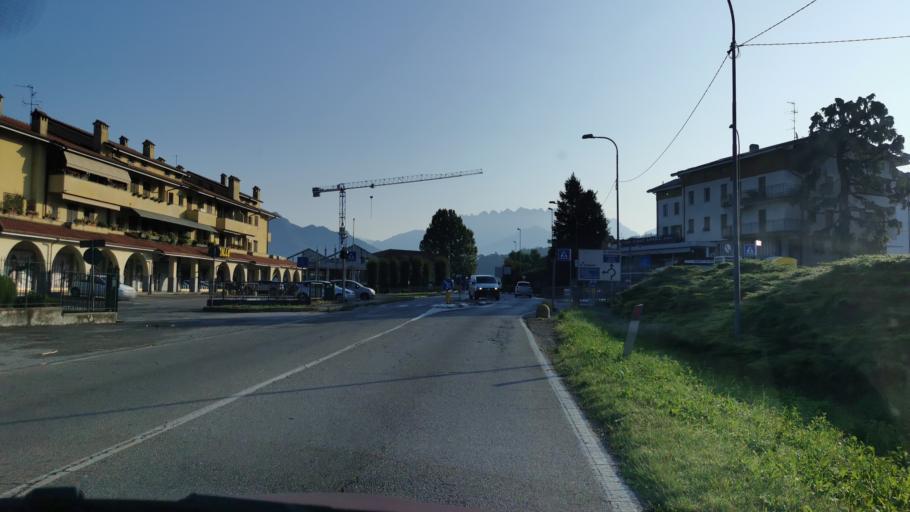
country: IT
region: Lombardy
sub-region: Provincia di Lecco
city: Oggiono
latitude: 45.7835
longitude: 9.3405
